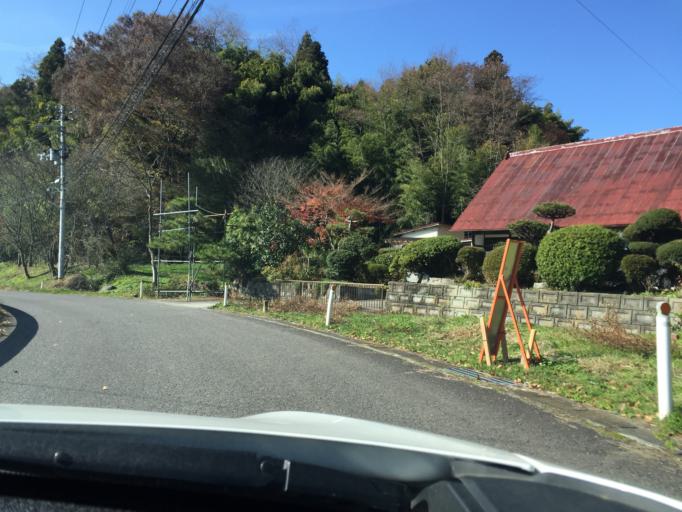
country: JP
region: Fukushima
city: Miharu
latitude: 37.4160
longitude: 140.4981
